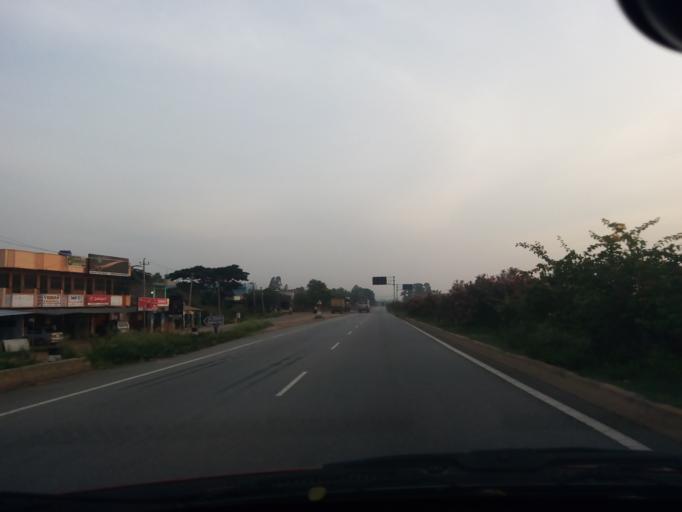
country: IN
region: Karnataka
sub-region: Chikkaballapur
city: Chik Ballapur
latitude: 13.3711
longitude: 77.7259
